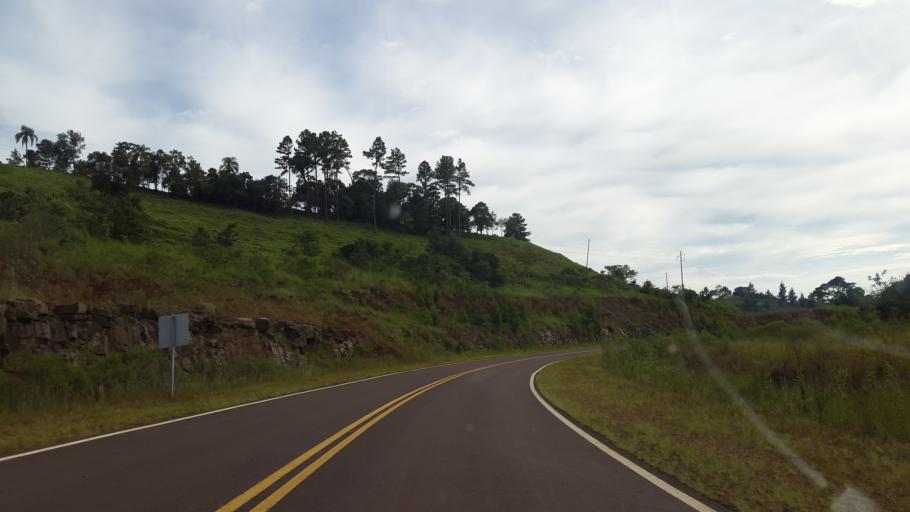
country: AR
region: Misiones
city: Bernardo de Irigoyen
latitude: -26.3968
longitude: -53.8158
